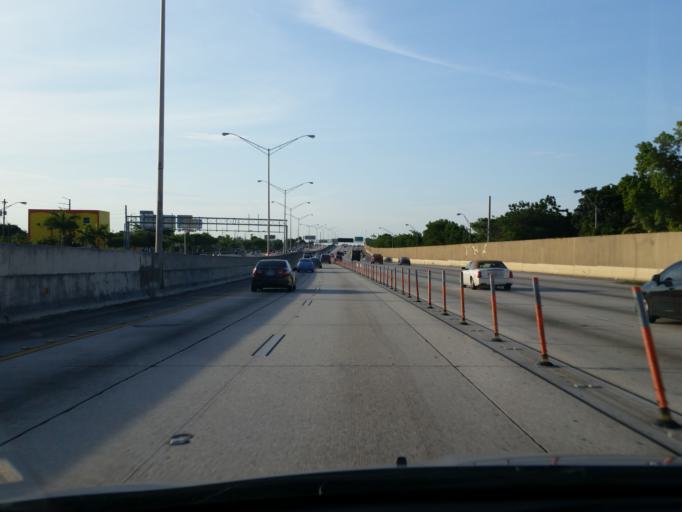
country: US
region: Florida
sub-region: Miami-Dade County
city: Pinewood
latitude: 25.8710
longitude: -80.2085
